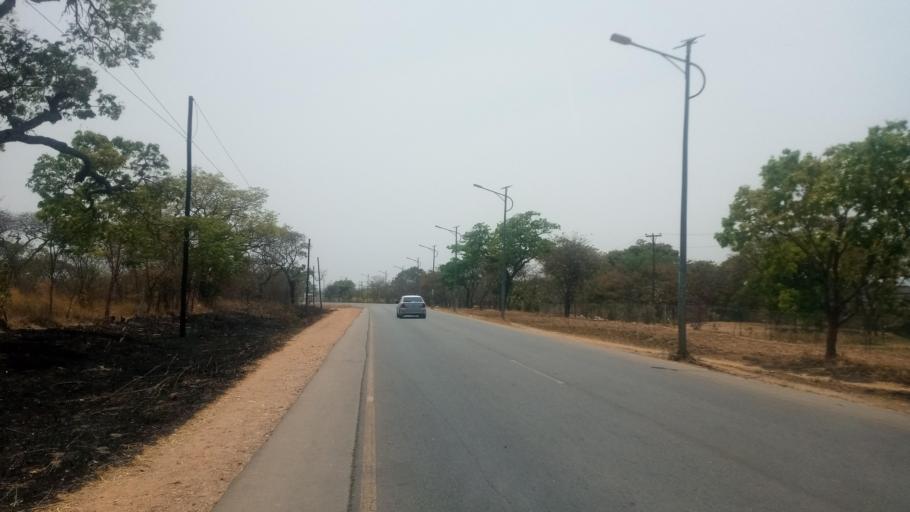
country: ZM
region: Lusaka
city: Lusaka
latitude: -15.4674
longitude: 28.4300
